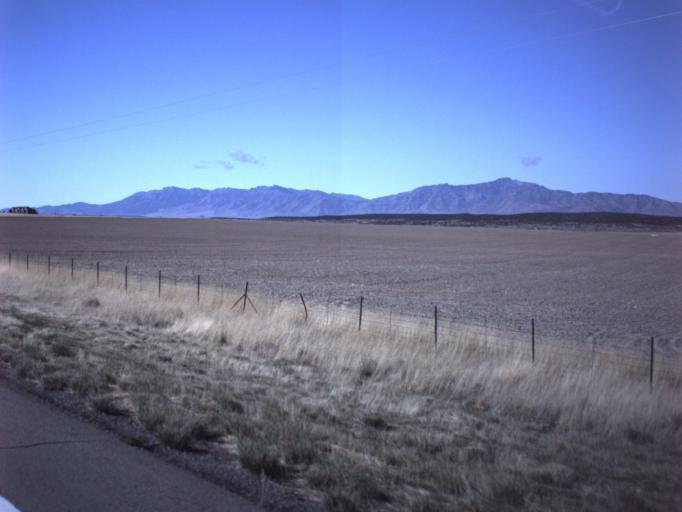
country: US
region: Utah
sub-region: Juab County
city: Nephi
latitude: 39.4520
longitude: -111.9088
